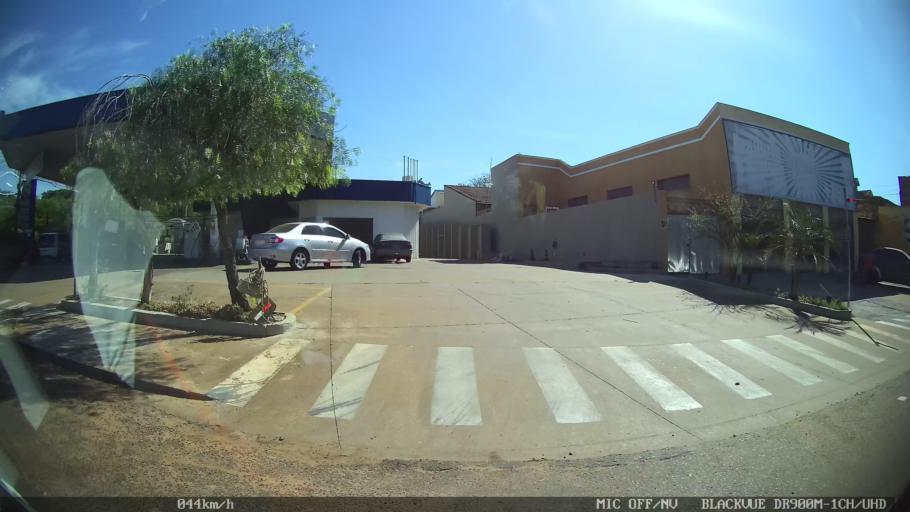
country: BR
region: Sao Paulo
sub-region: Sao Jose Do Rio Preto
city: Sao Jose do Rio Preto
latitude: -20.7767
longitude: -49.3819
